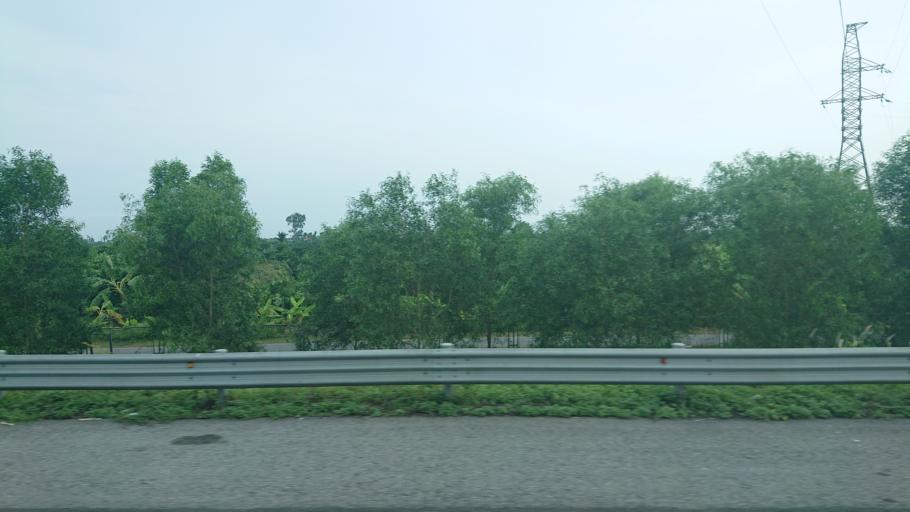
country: VN
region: Hai Duong
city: Tu Ky
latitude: 20.8303
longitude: 106.4494
